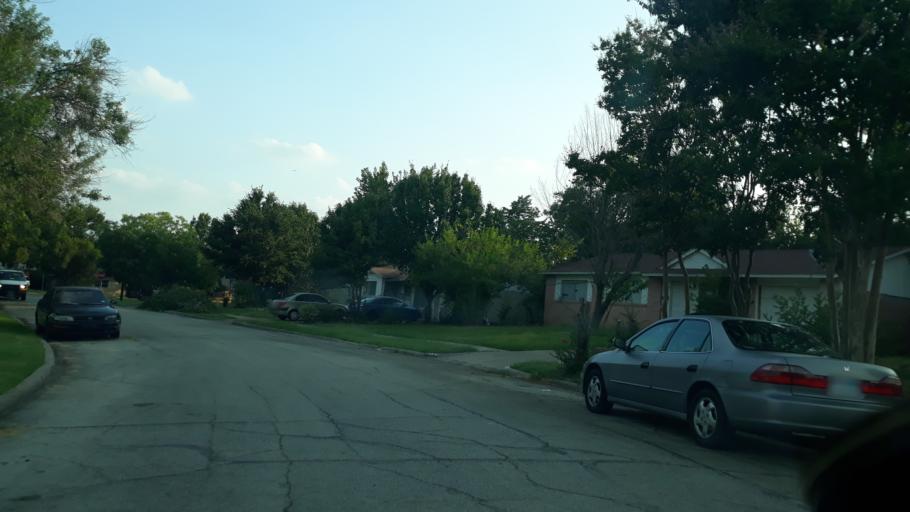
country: US
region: Texas
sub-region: Dallas County
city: Irving
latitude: 32.8483
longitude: -96.9831
